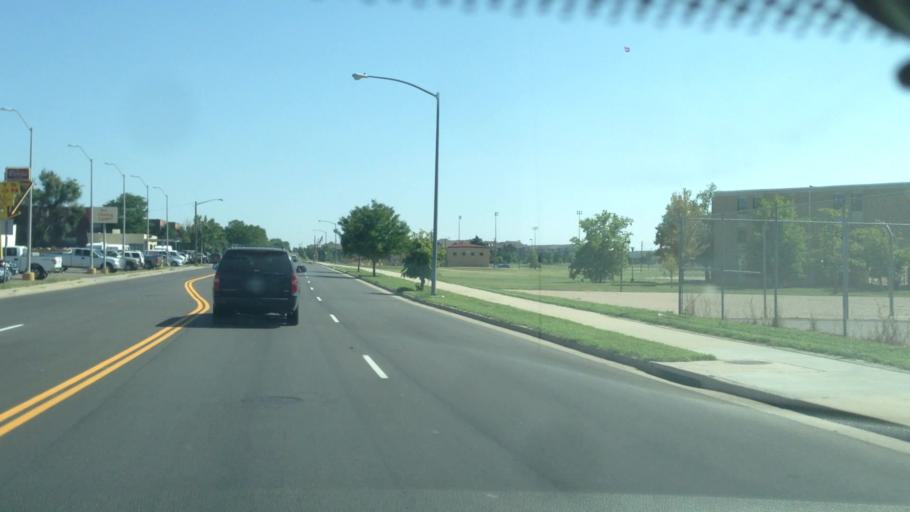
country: US
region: Colorado
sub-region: Adams County
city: Aurora
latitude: 39.7305
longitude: -104.8754
